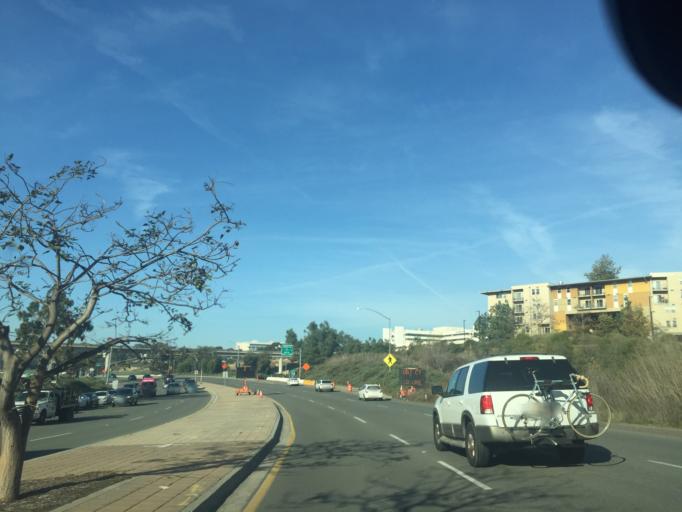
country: US
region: California
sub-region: San Diego County
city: La Jolla
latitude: 32.8721
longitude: -117.2261
